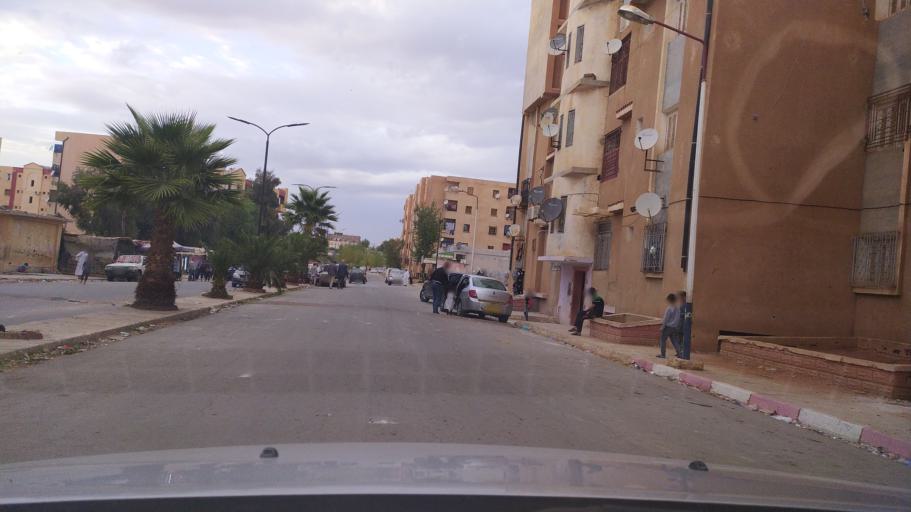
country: DZ
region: Tiaret
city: Frenda
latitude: 35.0563
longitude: 1.0616
